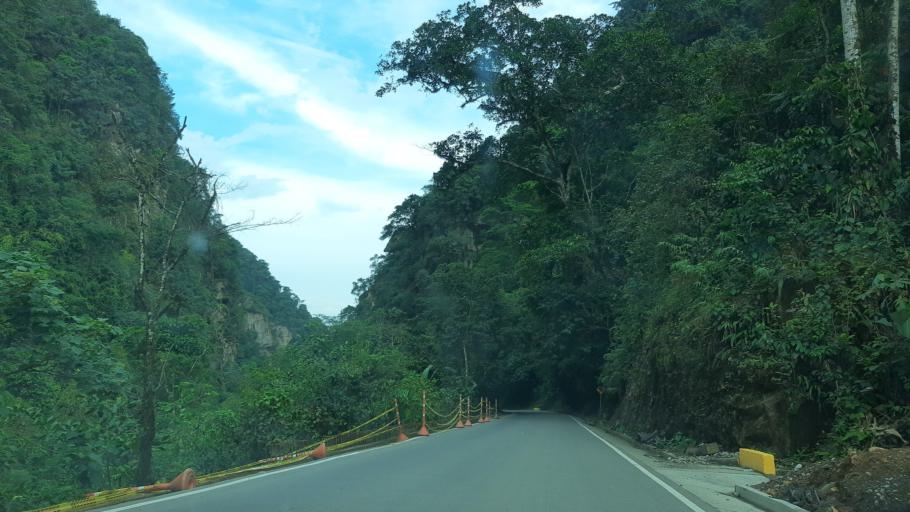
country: CO
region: Boyaca
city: Santa Maria
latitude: 4.8531
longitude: -73.2307
